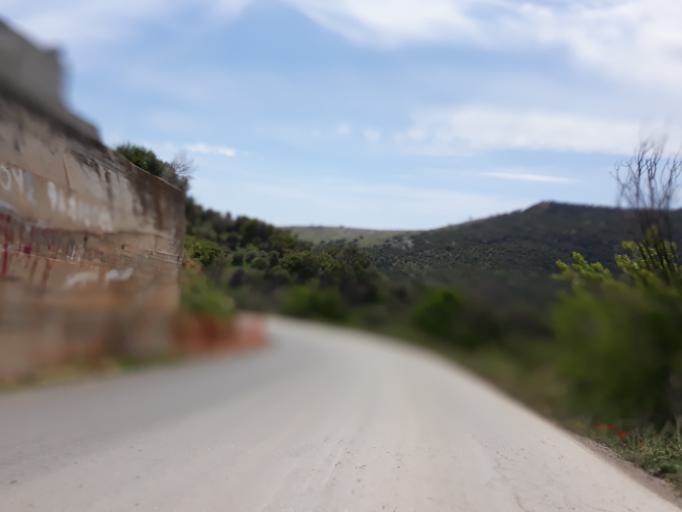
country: GR
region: Attica
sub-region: Nomarchia Dytikis Attikis
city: Magoula
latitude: 38.1480
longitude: 23.5243
